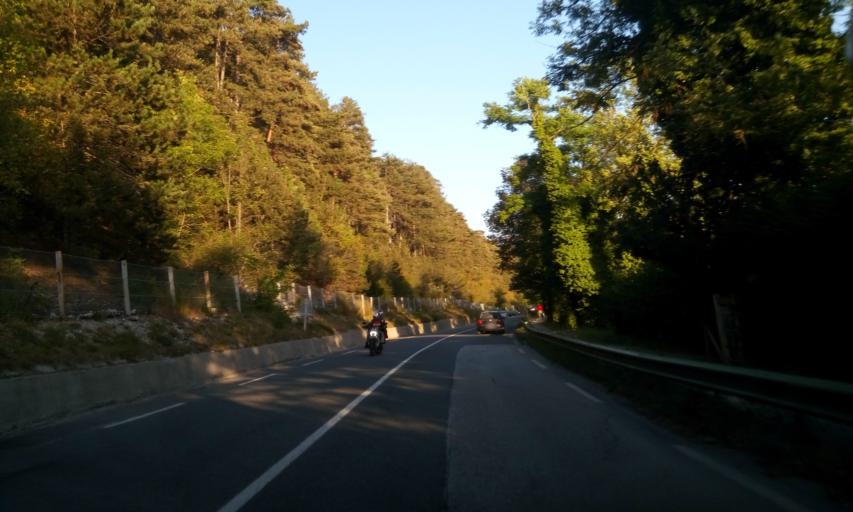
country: FR
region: Rhone-Alpes
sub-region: Departement de l'Ain
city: Montreal-la-Cluse
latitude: 46.1670
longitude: 5.5799
